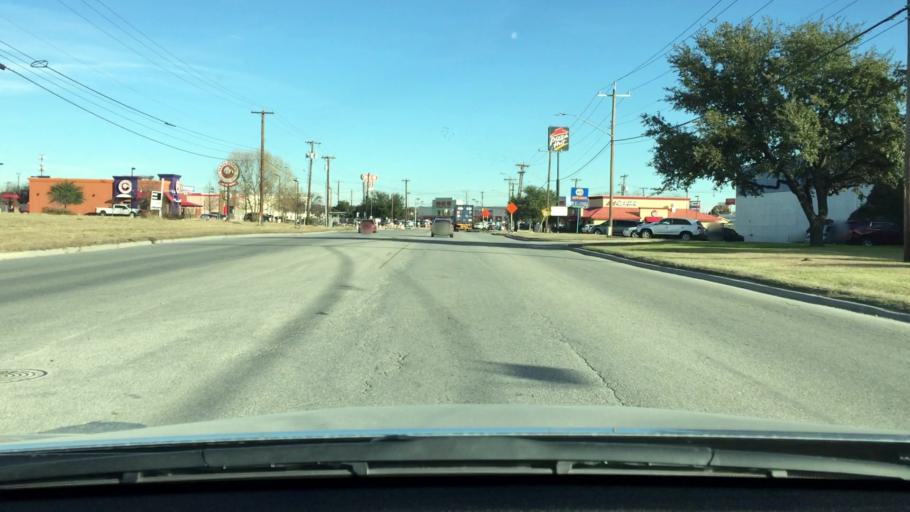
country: US
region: Texas
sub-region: Bexar County
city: Kirby
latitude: 29.4811
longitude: -98.3639
